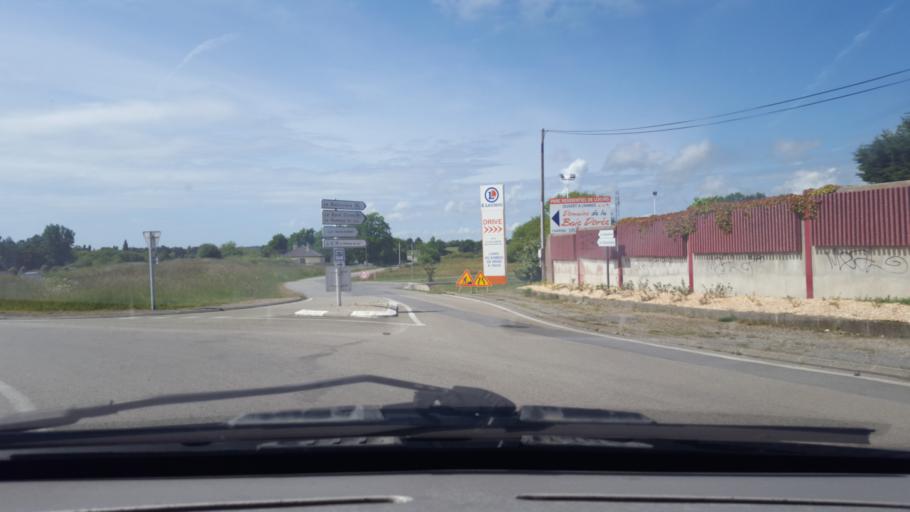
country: FR
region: Pays de la Loire
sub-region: Departement de la Loire-Atlantique
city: Bourgneuf-en-Retz
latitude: 47.0511
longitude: -1.9632
